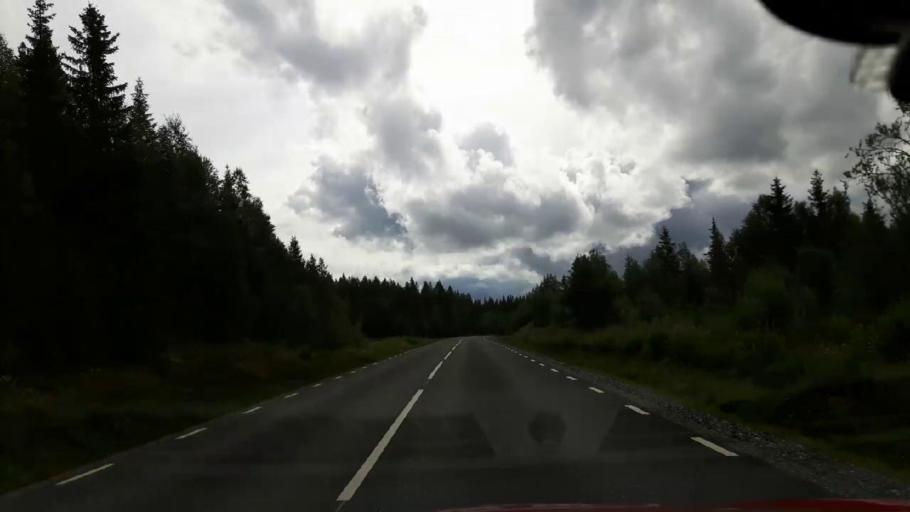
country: NO
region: Nord-Trondelag
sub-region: Lierne
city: Sandvika
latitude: 64.6006
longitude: 14.1206
